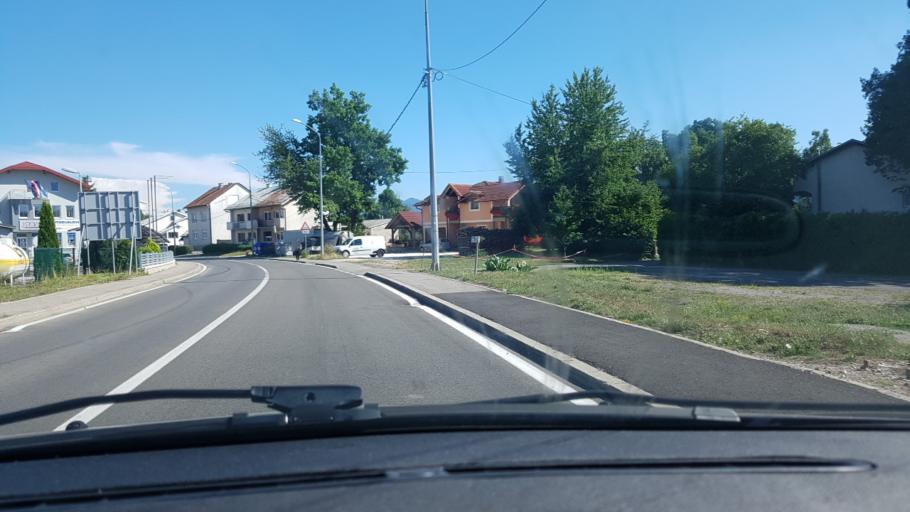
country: HR
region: Licko-Senjska
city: Gospic
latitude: 44.5430
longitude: 15.3741
